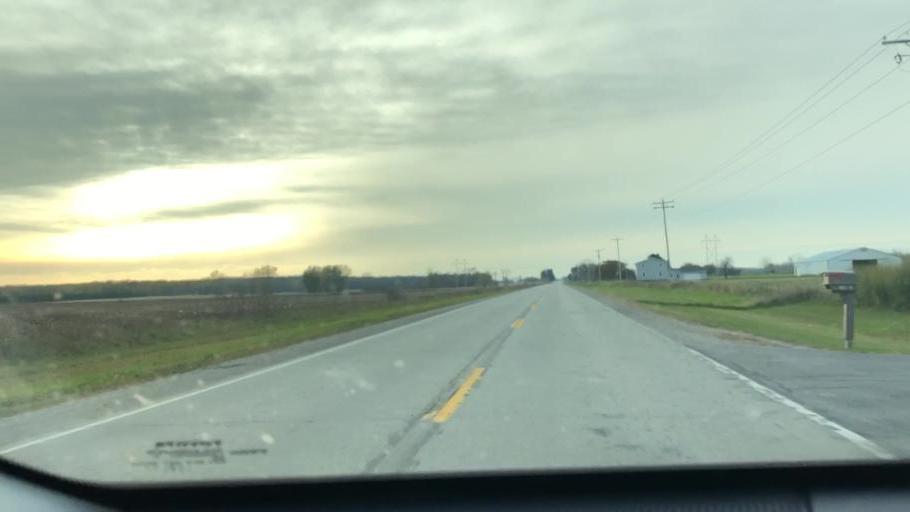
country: US
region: Wisconsin
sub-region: Outagamie County
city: Seymour
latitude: 44.4438
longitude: -88.3061
